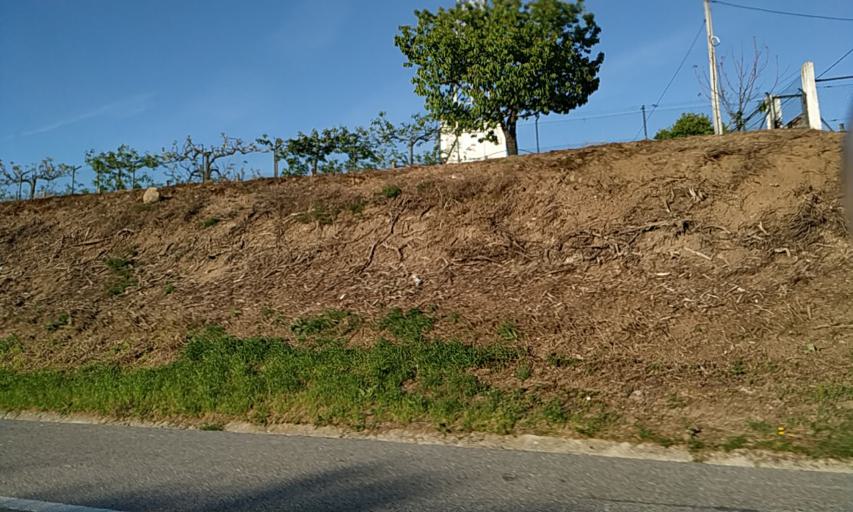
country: PT
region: Braga
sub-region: Vila Nova de Famalicao
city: Vila Nova de Famalicao
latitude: 41.4226
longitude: -8.4941
